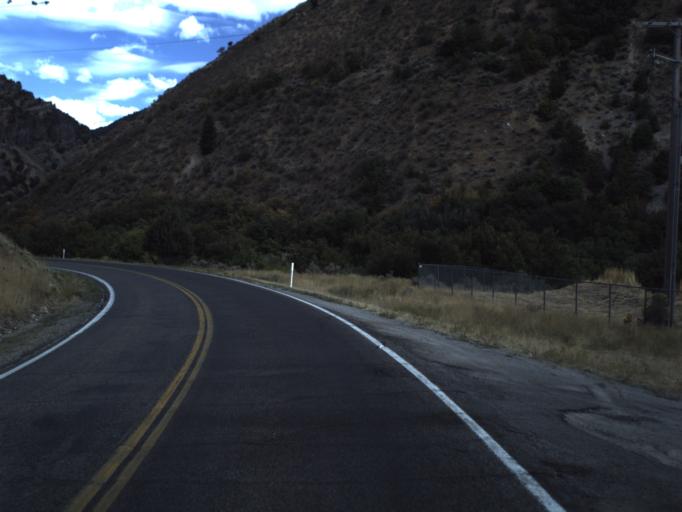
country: US
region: Utah
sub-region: Cache County
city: Hyrum
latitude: 41.6252
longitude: -111.7955
